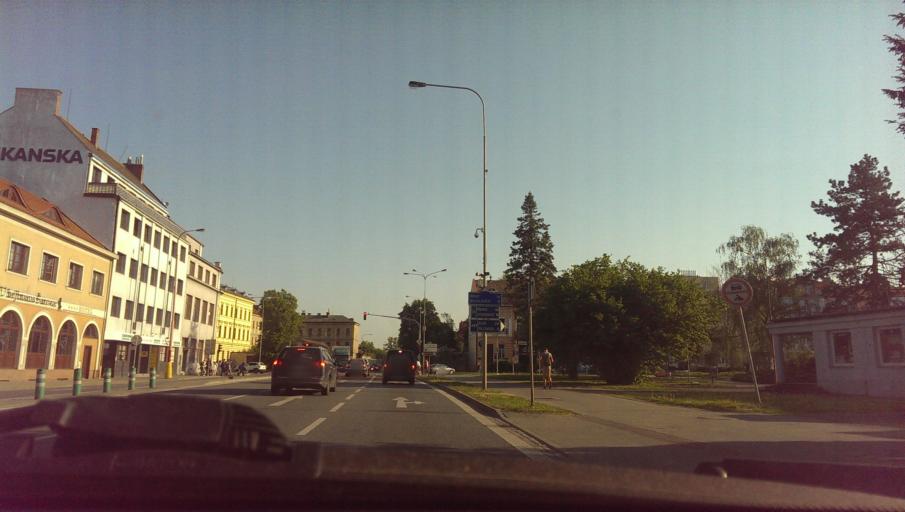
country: CZ
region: Zlin
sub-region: Okres Uherske Hradiste
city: Uherske Hradiste
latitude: 49.0673
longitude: 17.4665
